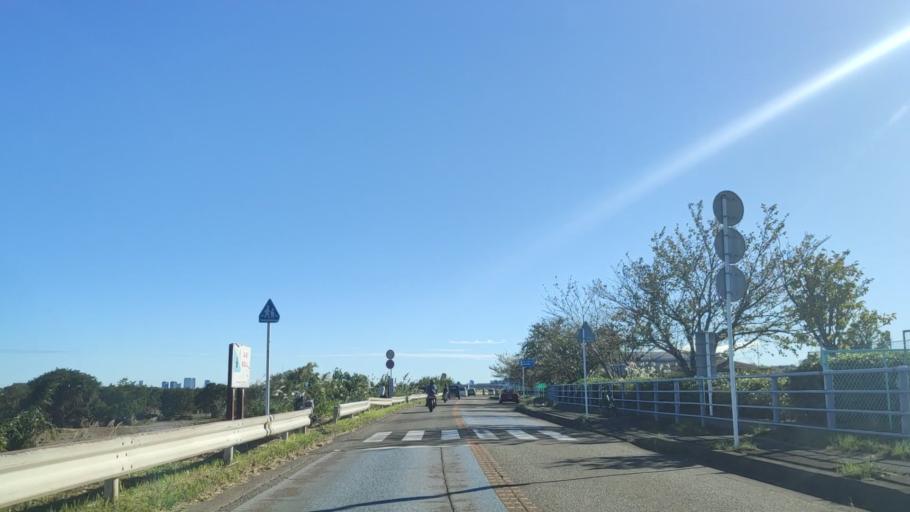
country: JP
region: Kanagawa
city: Zama
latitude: 35.5089
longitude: 139.3741
